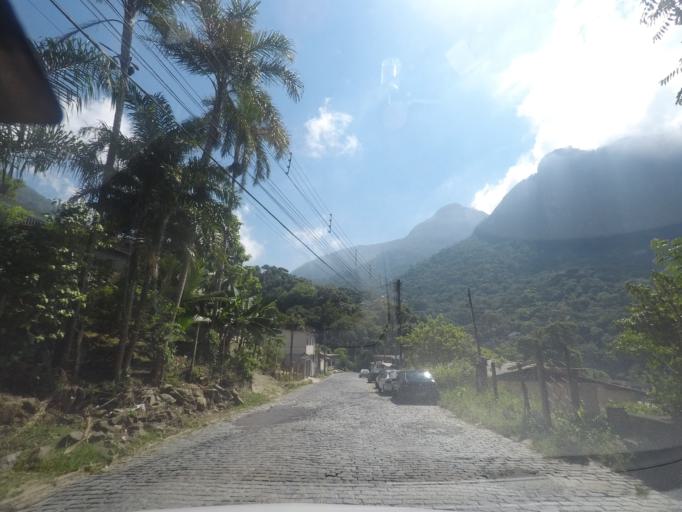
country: BR
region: Rio de Janeiro
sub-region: Petropolis
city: Petropolis
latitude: -22.5471
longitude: -43.1797
